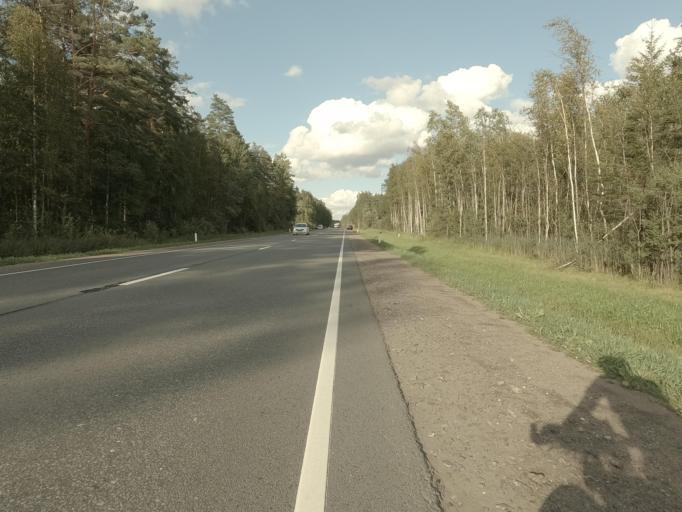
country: RU
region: Leningrad
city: Mga
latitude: 59.7104
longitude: 31.0234
